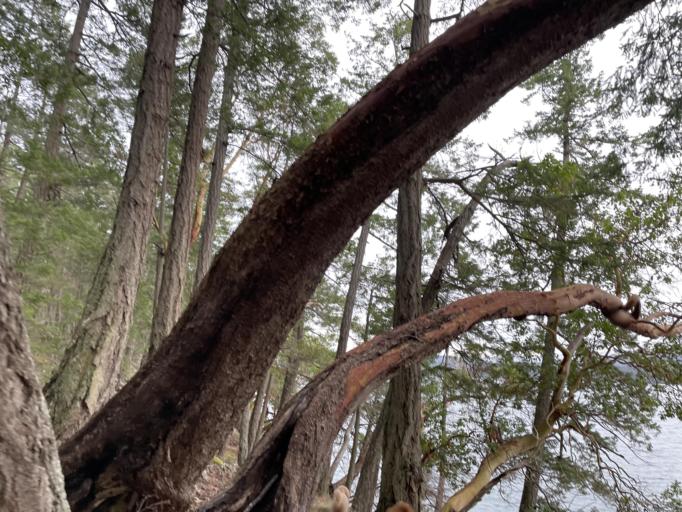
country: CA
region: British Columbia
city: North Cowichan
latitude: 48.9389
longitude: -123.5499
